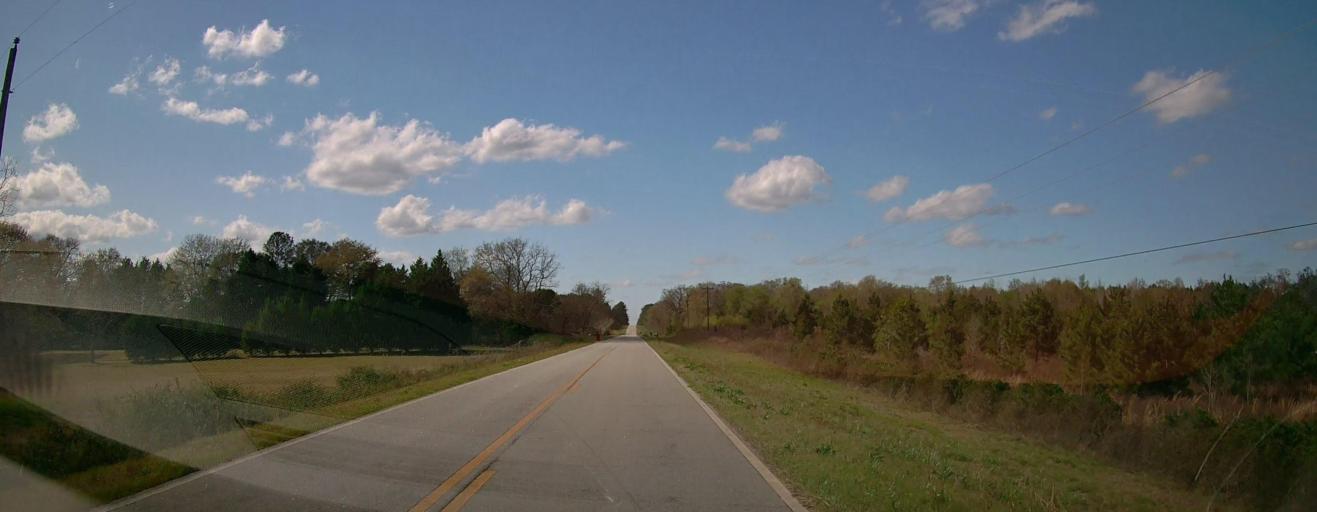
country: US
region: Georgia
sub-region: Wilkinson County
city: Gordon
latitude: 32.8321
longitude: -83.4304
